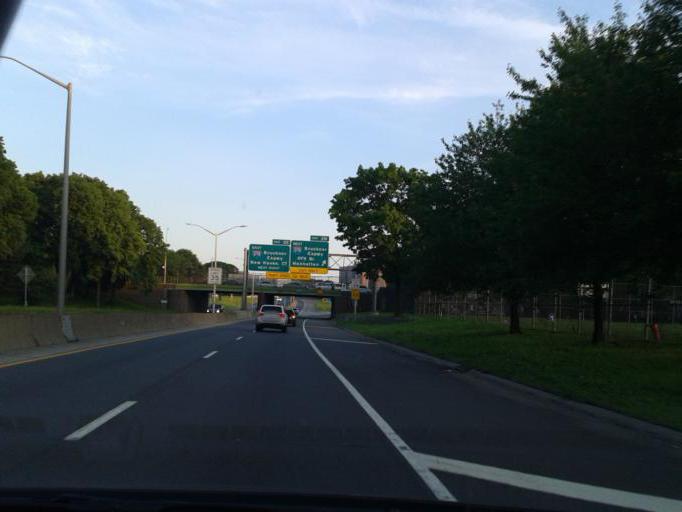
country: US
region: New York
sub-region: Bronx
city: The Bronx
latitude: 40.8280
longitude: -73.8730
